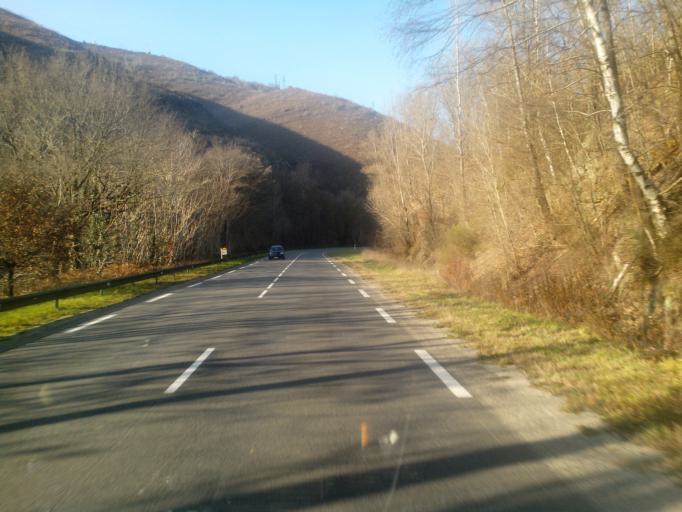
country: FR
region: Midi-Pyrenees
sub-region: Departement de l'Aveyron
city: Viviez
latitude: 44.5684
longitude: 2.2095
